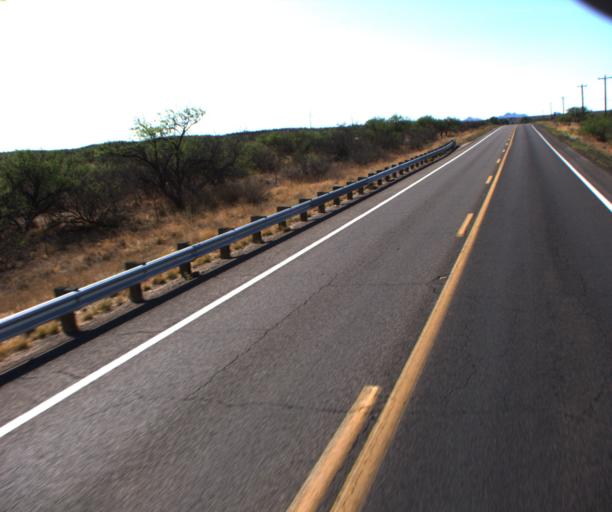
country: US
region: Arizona
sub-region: Cochise County
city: Saint David
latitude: 31.8558
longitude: -110.2017
